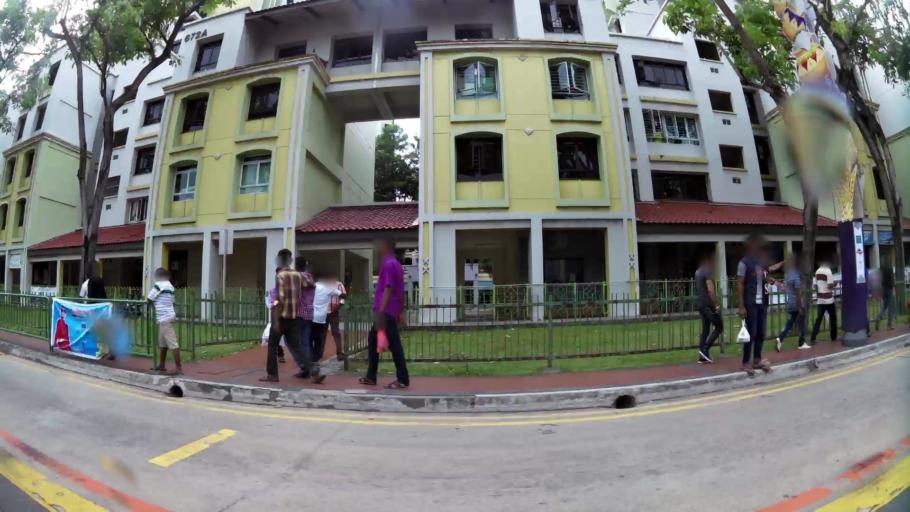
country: SG
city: Singapore
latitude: 1.3084
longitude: 103.8530
